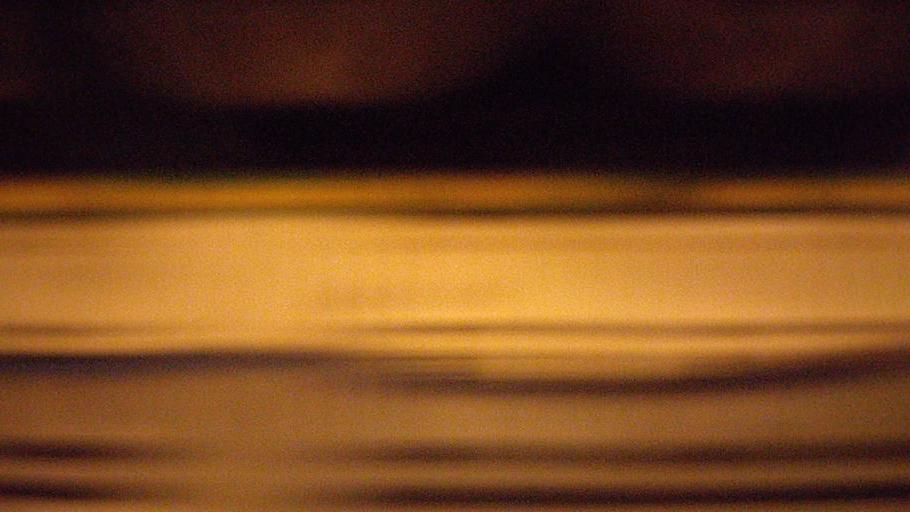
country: TH
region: Sing Buri
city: Phrom Buri
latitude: 14.7735
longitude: 100.4513
